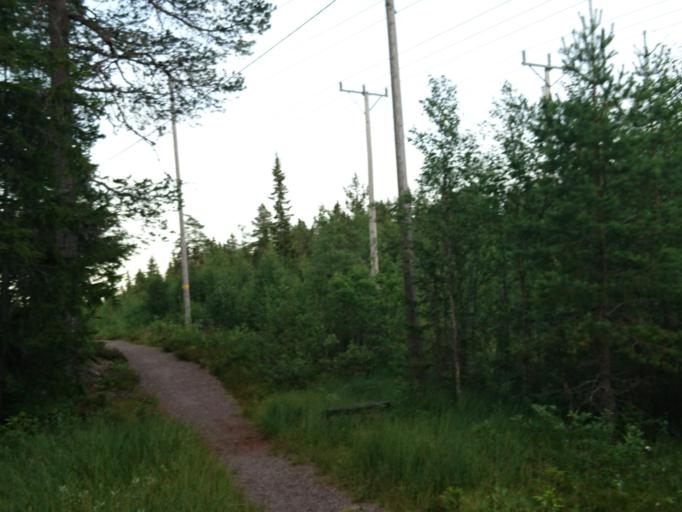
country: SE
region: Dalarna
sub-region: Malung-Saelens kommun
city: Malung
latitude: 61.1702
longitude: 13.1724
